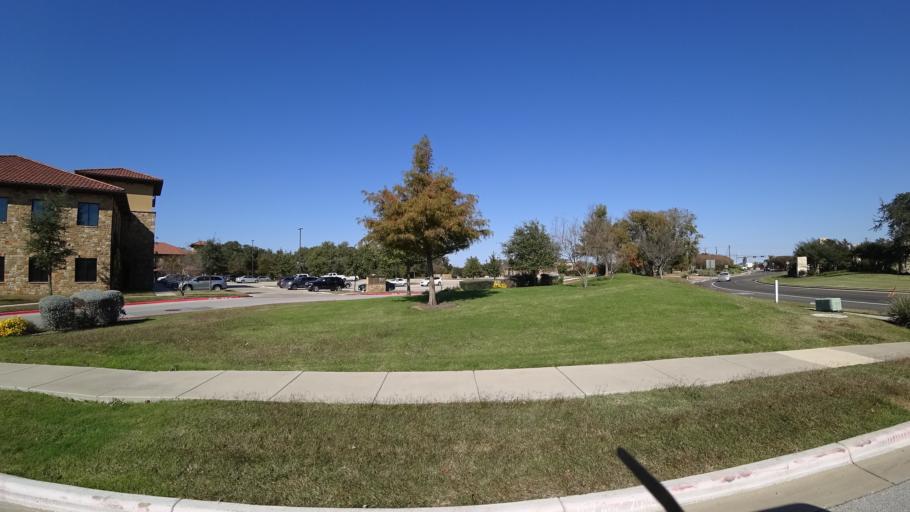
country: US
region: Texas
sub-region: Williamson County
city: Anderson Mill
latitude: 30.3932
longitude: -97.8469
